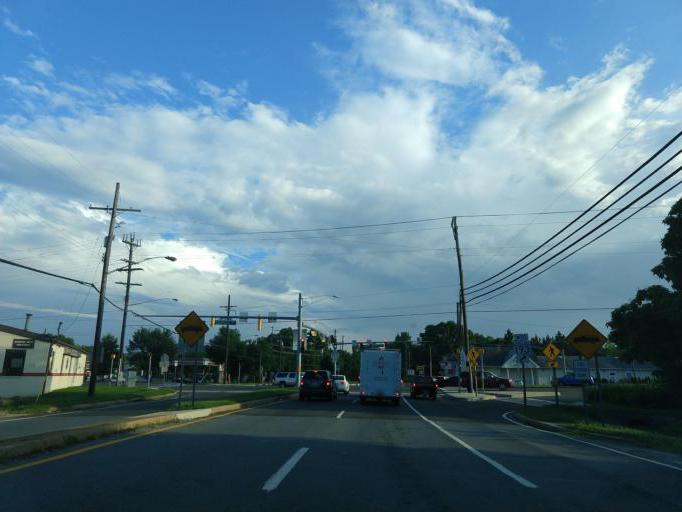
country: US
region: Maryland
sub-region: Prince George's County
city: Berwyn Heights
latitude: 38.9997
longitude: -76.9252
